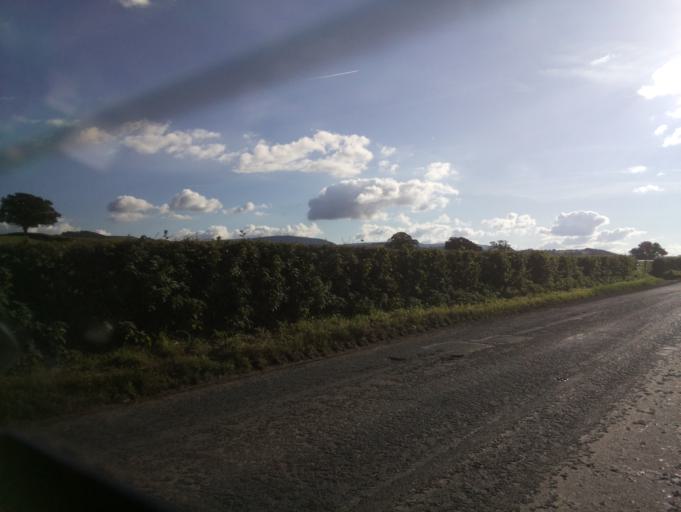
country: GB
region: England
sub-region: Herefordshire
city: Clifford
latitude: 52.0939
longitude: -3.1119
